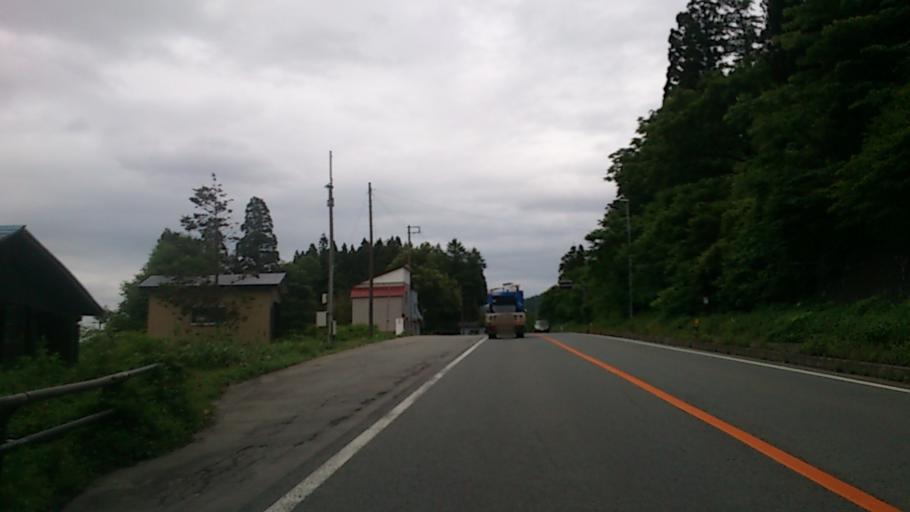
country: JP
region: Yamagata
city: Shinjo
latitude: 38.7430
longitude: 140.1254
